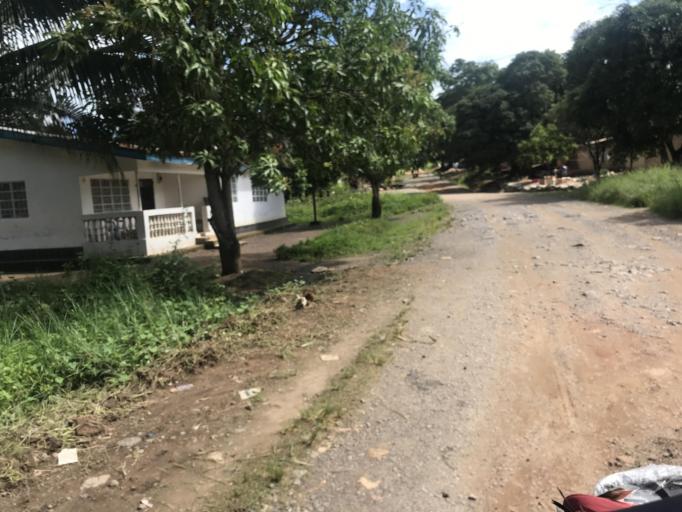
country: SL
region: Eastern Province
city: Koidu
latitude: 8.6449
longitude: -10.9867
